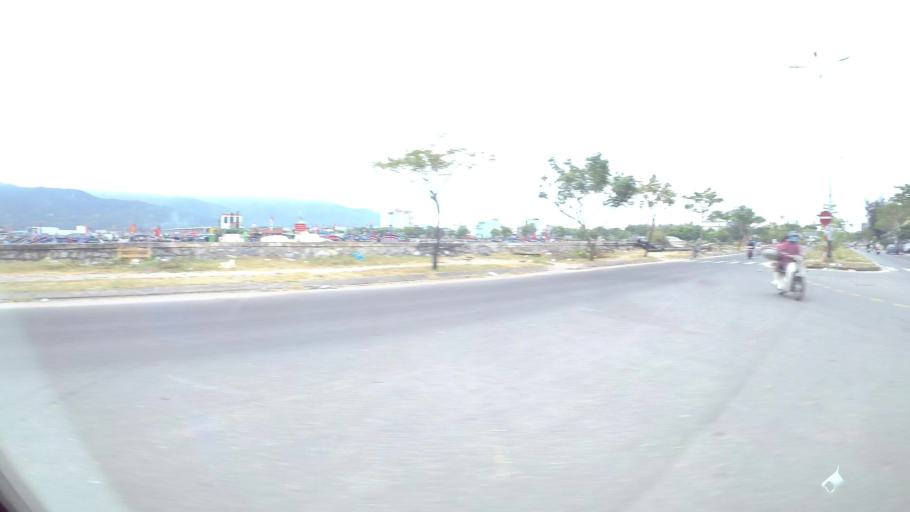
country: VN
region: Da Nang
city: Da Nang
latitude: 16.0934
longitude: 108.2355
